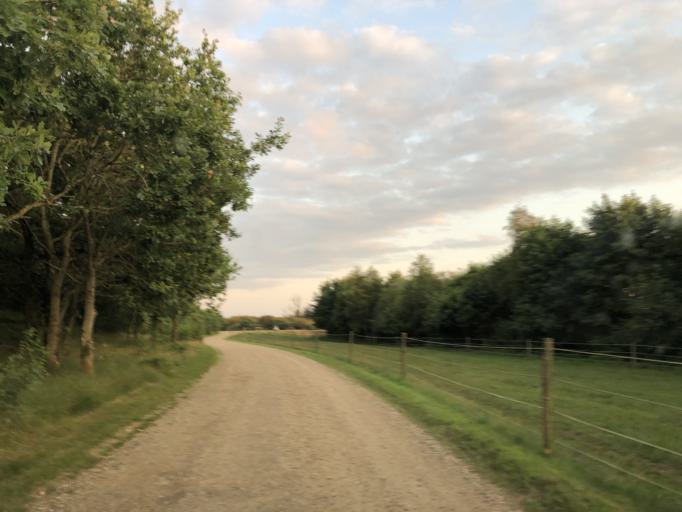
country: DK
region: Central Jutland
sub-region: Holstebro Kommune
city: Vinderup
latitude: 56.4616
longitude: 8.8963
